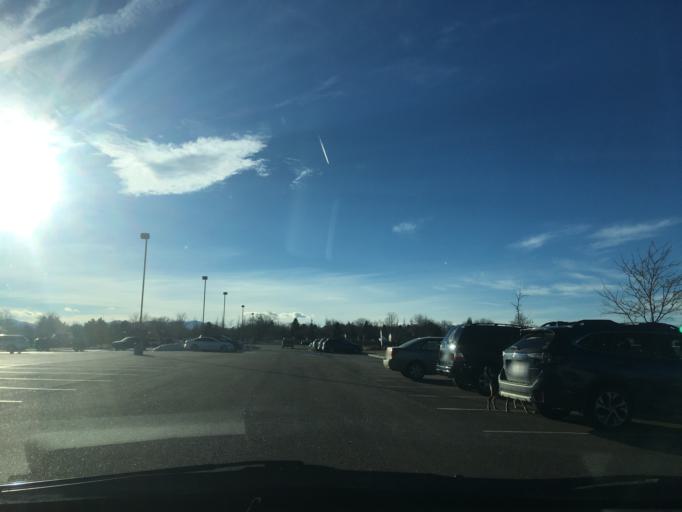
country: US
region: Colorado
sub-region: Broomfield County
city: Broomfield
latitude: 39.9390
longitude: -105.0498
